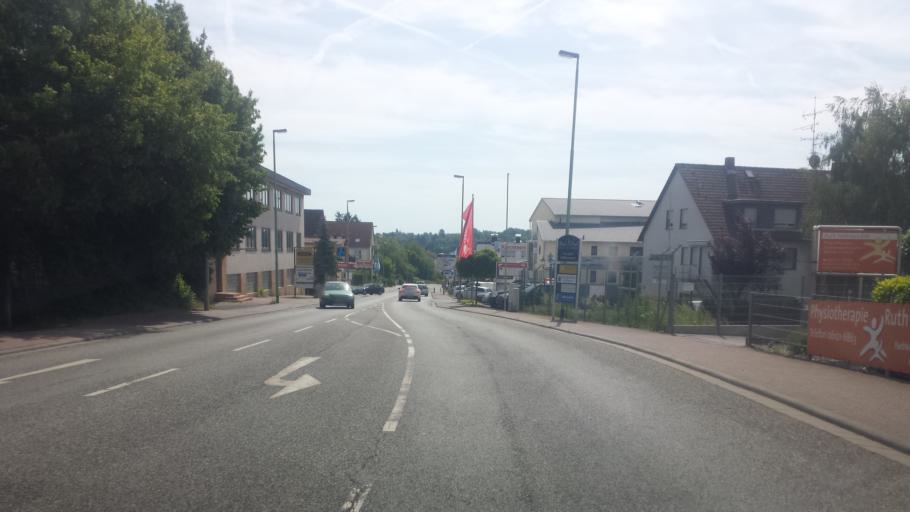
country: DE
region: Hesse
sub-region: Regierungsbezirk Darmstadt
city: Bad Vilbel
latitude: 50.1878
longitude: 8.7307
